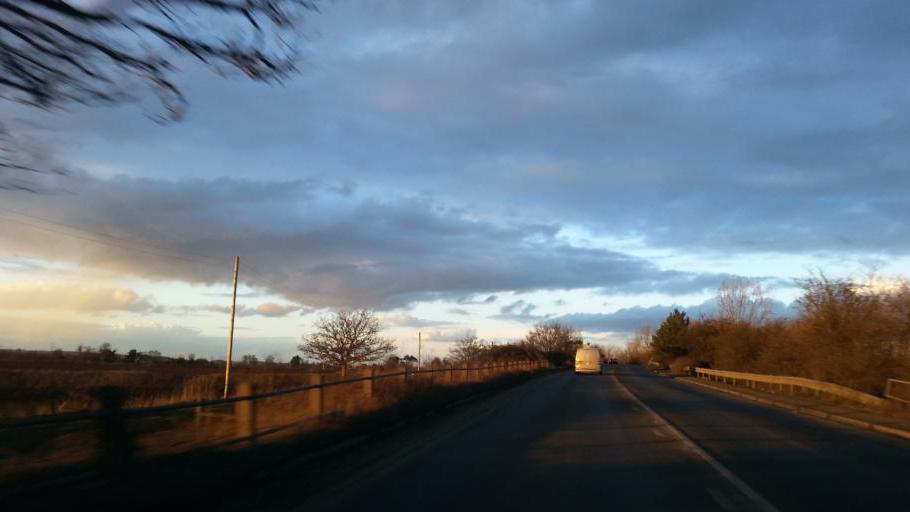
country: GB
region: England
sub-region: Nottinghamshire
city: Newark on Trent
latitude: 53.1162
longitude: -0.8201
